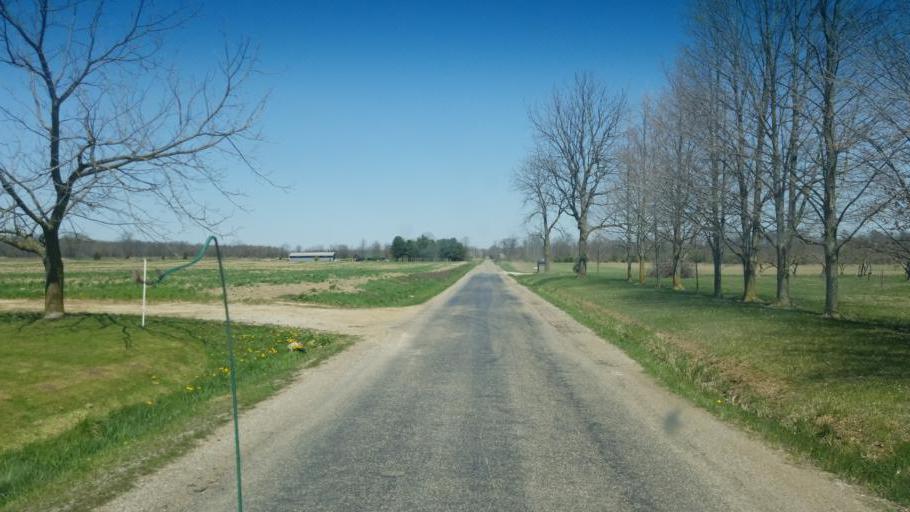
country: US
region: Ohio
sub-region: Huron County
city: New London
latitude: 41.0300
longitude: -82.4349
